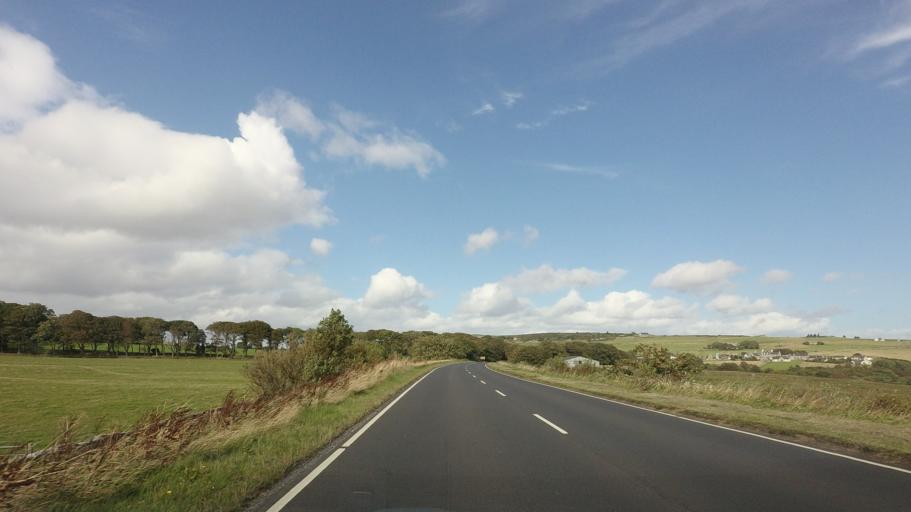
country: GB
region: Scotland
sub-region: Highland
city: Wick
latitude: 58.2707
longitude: -3.3929
